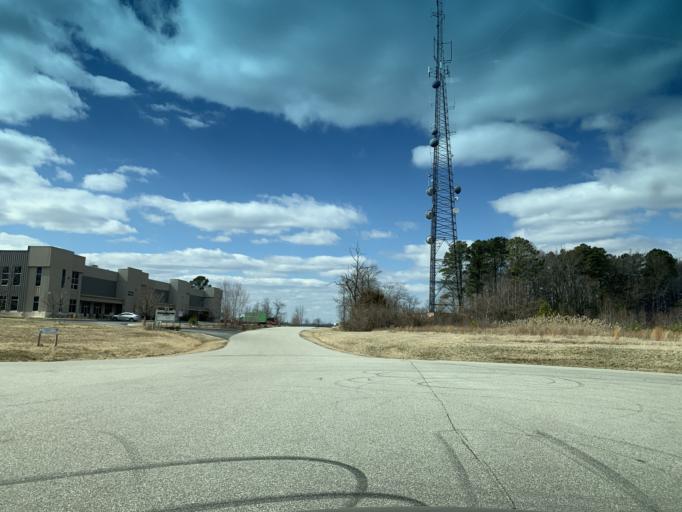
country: US
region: Maryland
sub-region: Queen Anne's County
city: Stevensville
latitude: 38.9548
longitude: -76.3509
